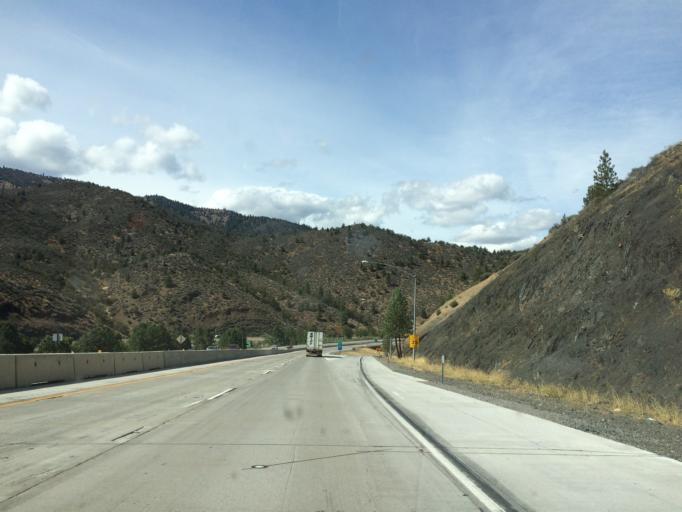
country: US
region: California
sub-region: Siskiyou County
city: Montague
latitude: 41.8517
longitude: -122.5695
